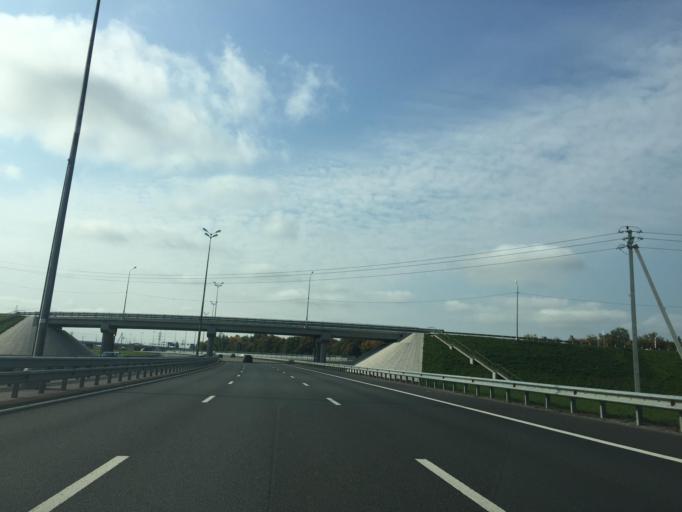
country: RU
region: Leningrad
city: Mariyenburg
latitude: 59.5242
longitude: 30.0755
